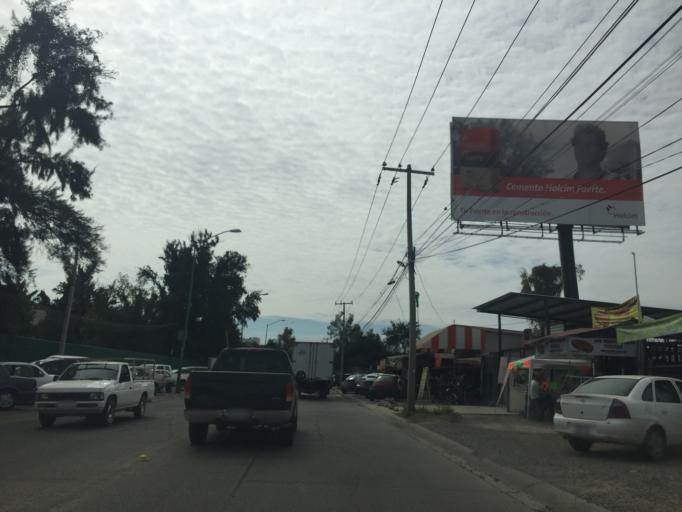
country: MX
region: Guanajuato
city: Leon
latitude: 21.1660
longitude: -101.6849
